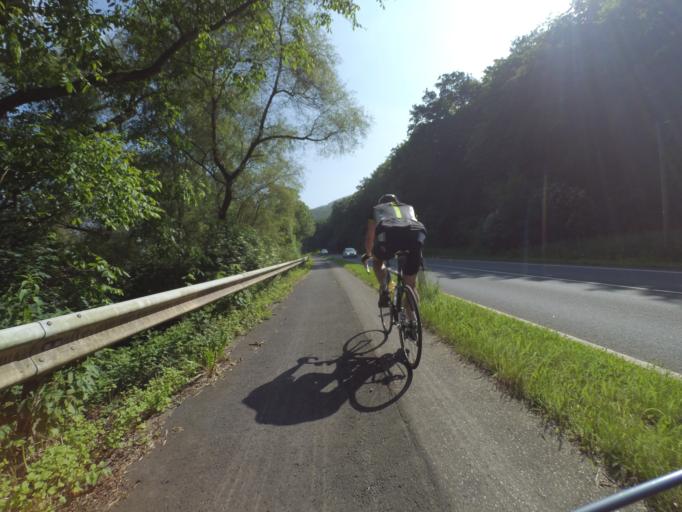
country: DE
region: Rheinland-Pfalz
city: Moselkern
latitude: 50.1851
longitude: 7.3644
